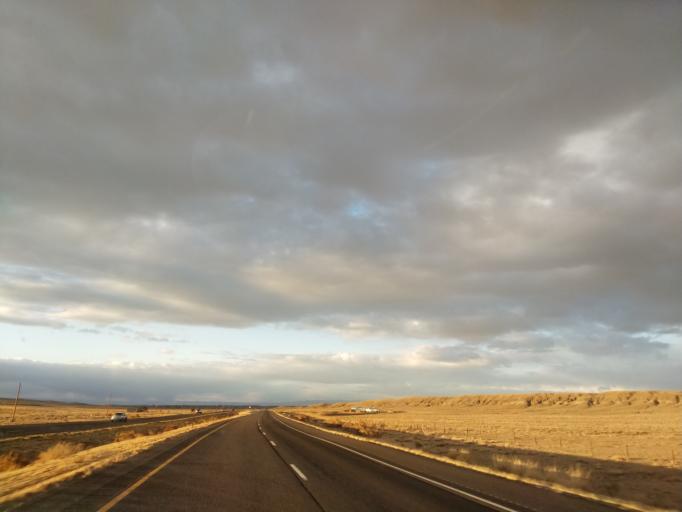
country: US
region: Colorado
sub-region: Mesa County
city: Palisade
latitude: 38.8838
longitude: -108.3554
